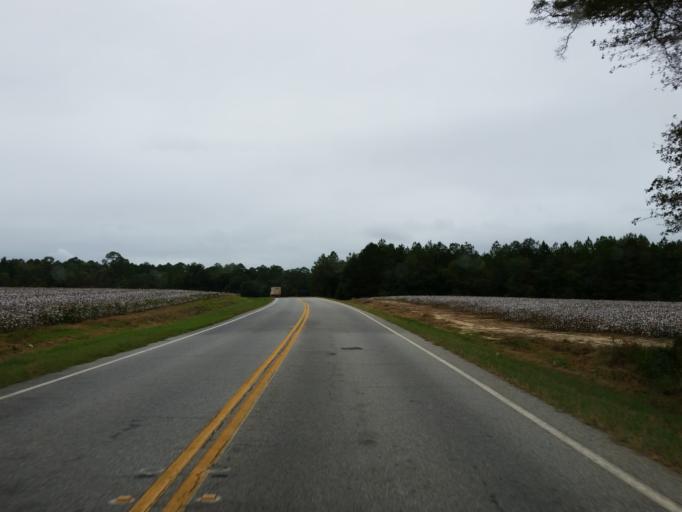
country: US
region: Georgia
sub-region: Cook County
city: Adel
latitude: 31.1296
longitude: -83.3392
